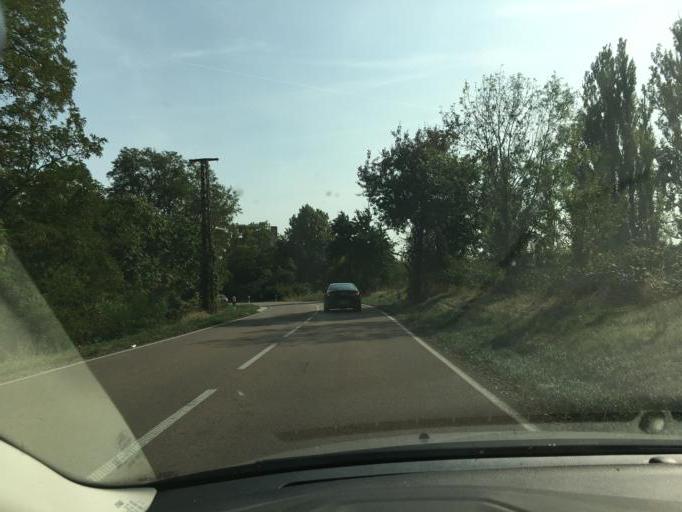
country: DE
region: Saxony-Anhalt
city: Nienburg/Saale
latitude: 51.8540
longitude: 11.7610
